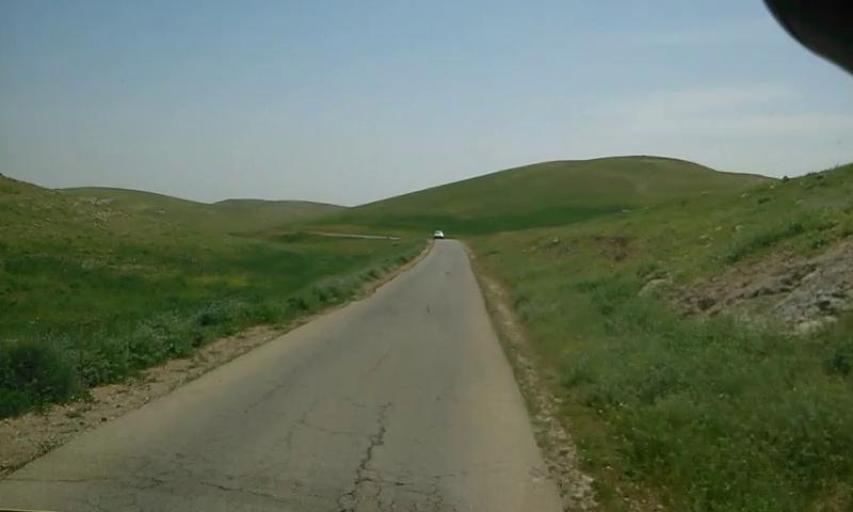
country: PS
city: `Arab ar Rashaydah
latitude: 31.5490
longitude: 35.2535
